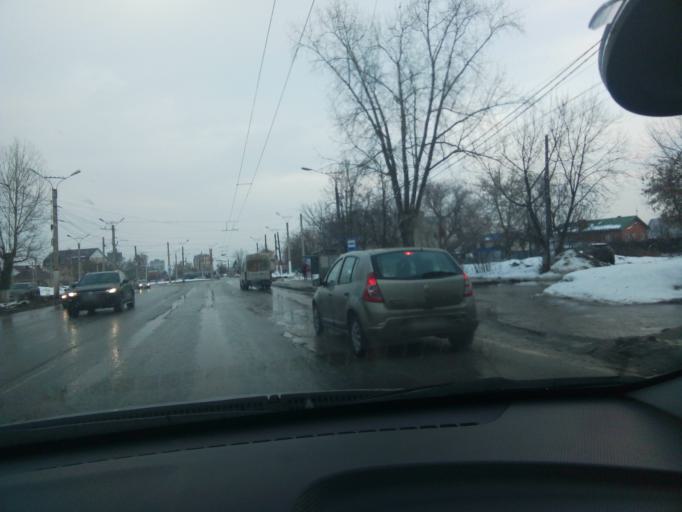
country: RU
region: Chuvashia
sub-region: Cheboksarskiy Rayon
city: Cheboksary
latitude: 56.1266
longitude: 47.2106
